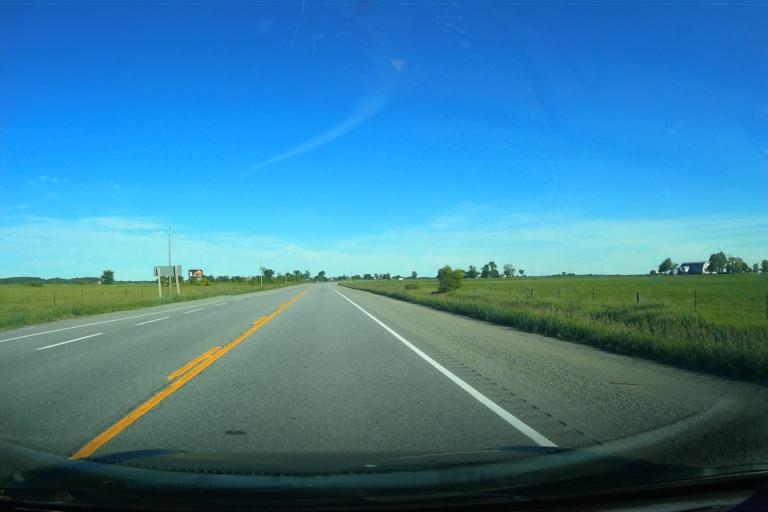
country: CA
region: Ontario
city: Pembroke
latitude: 45.6803
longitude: -76.9413
